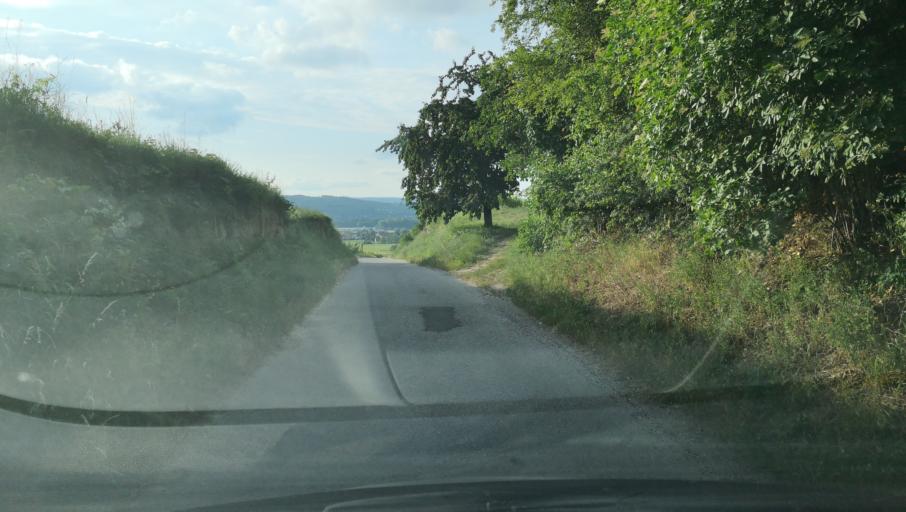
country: AT
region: Lower Austria
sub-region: Politischer Bezirk Krems
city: Paudorf
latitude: 48.3757
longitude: 15.6178
